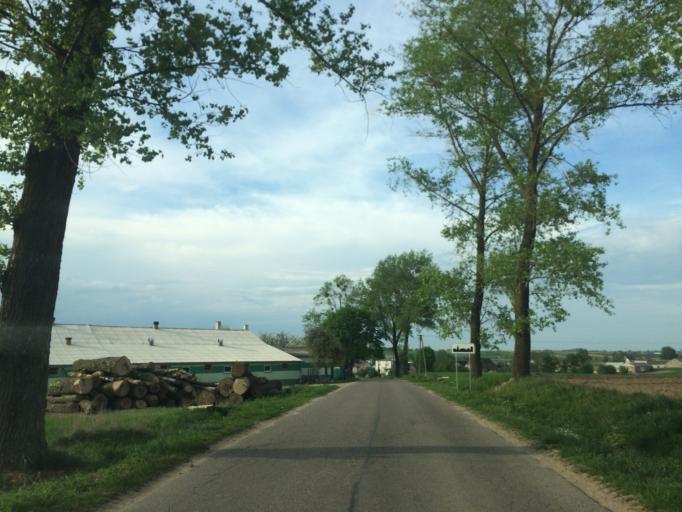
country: PL
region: Kujawsko-Pomorskie
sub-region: Powiat brodnicki
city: Brzozie
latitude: 53.3512
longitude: 19.6008
